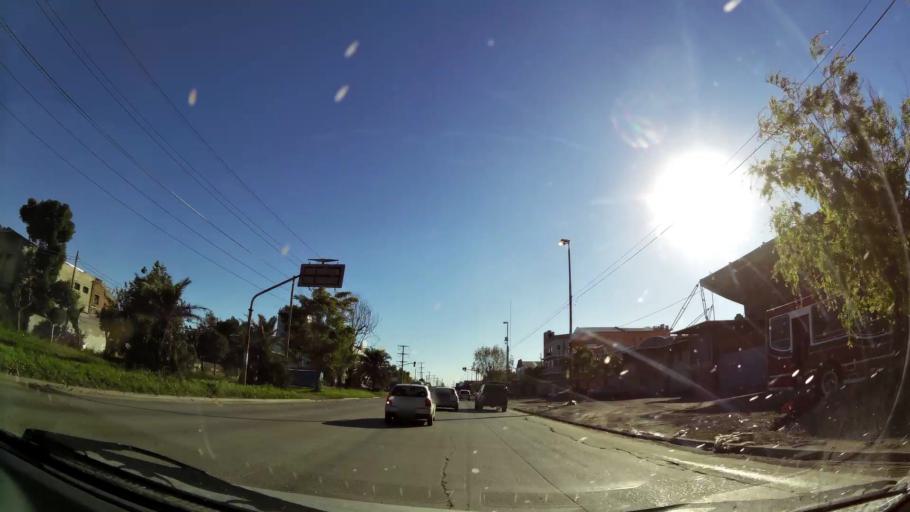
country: AR
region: Buenos Aires
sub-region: Partido de Quilmes
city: Quilmes
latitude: -34.7413
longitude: -58.3226
